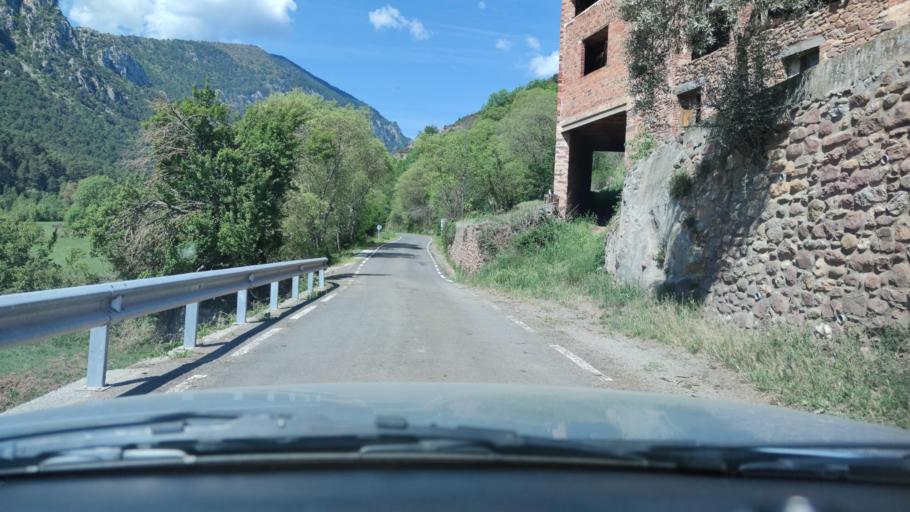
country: ES
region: Catalonia
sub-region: Provincia de Lleida
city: Coll de Nargo
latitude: 42.2931
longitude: 1.3448
